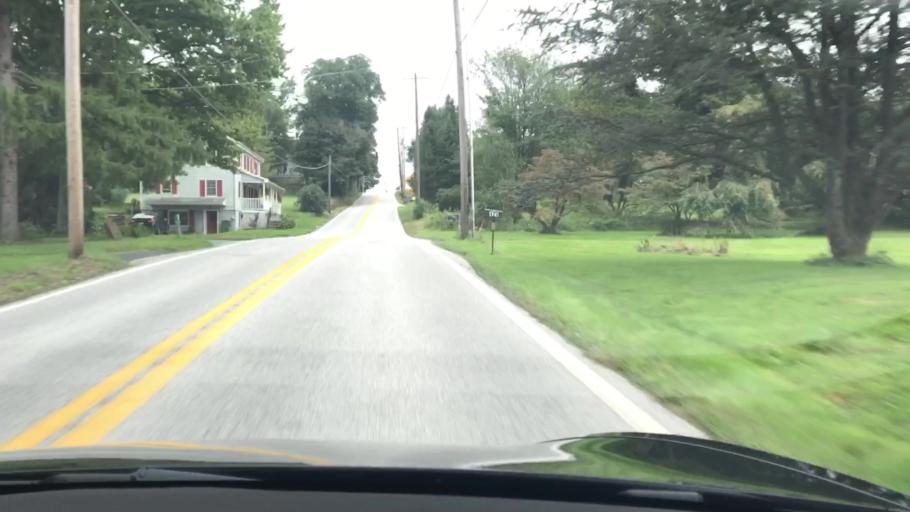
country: US
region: Pennsylvania
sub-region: York County
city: Dillsburg
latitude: 40.1384
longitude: -76.9640
